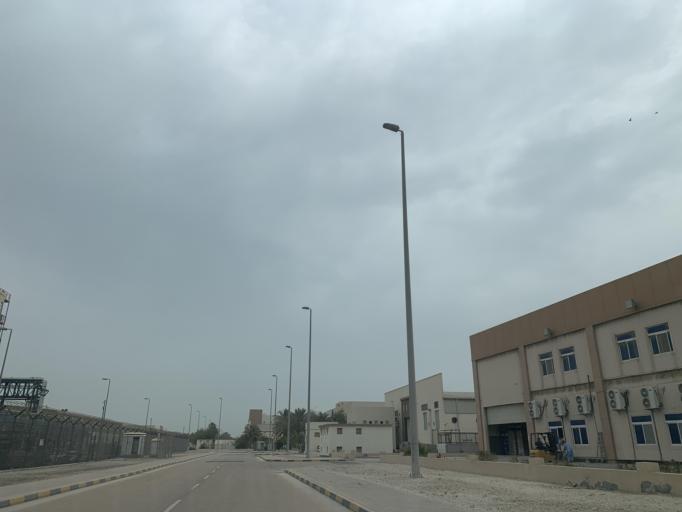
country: BH
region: Muharraq
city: Al Hadd
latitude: 26.2159
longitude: 50.6590
